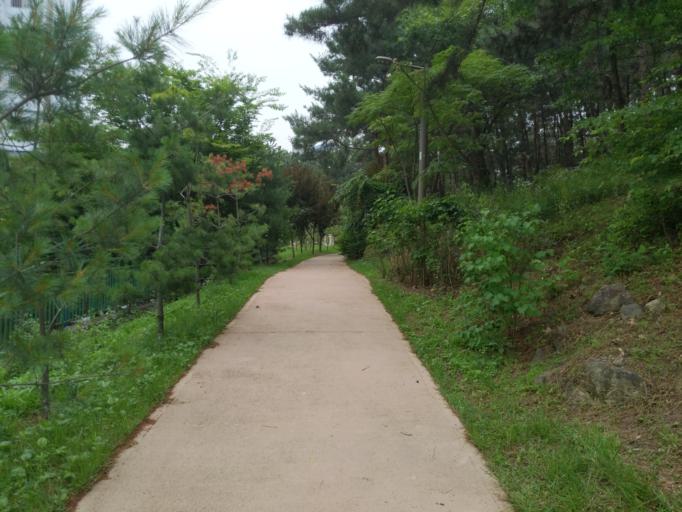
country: KR
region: Daegu
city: Hwawon
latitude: 35.8032
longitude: 128.5331
